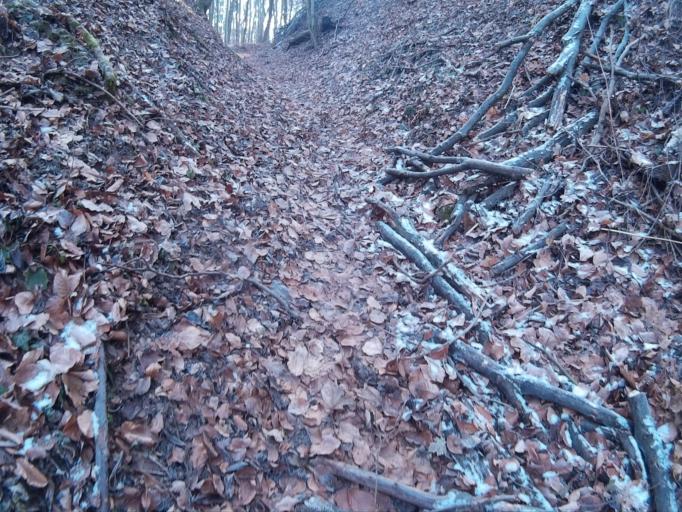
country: HU
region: Komarom-Esztergom
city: Tatabanya
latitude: 47.5119
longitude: 18.4138
